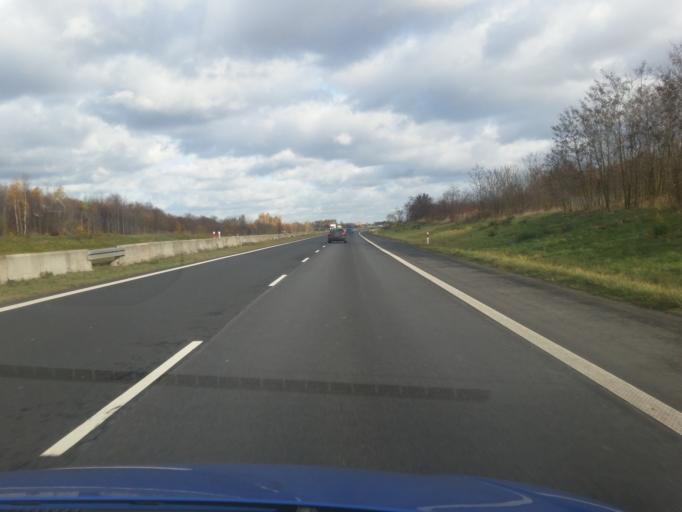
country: PL
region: Silesian Voivodeship
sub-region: Powiat czestochowski
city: Borowno
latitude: 50.9446
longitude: 19.2382
